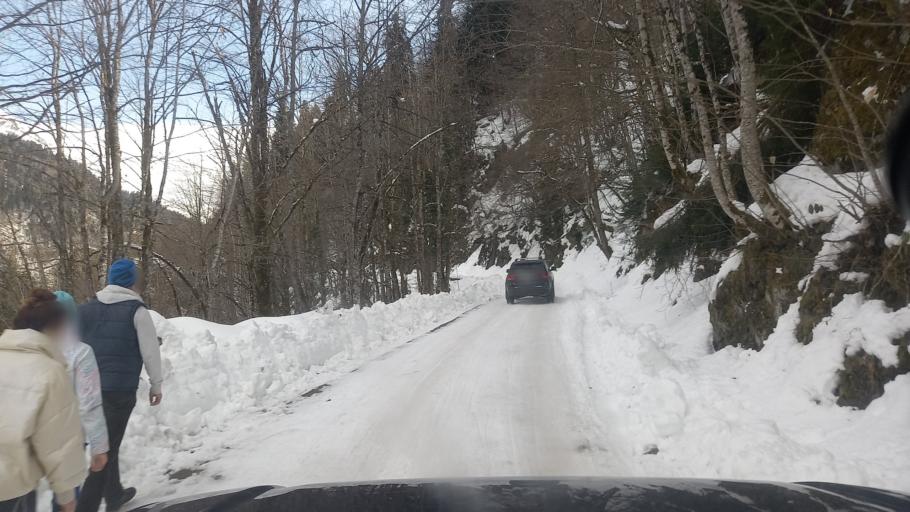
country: GE
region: Abkhazia
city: Gagra
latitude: 43.4762
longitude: 40.5405
